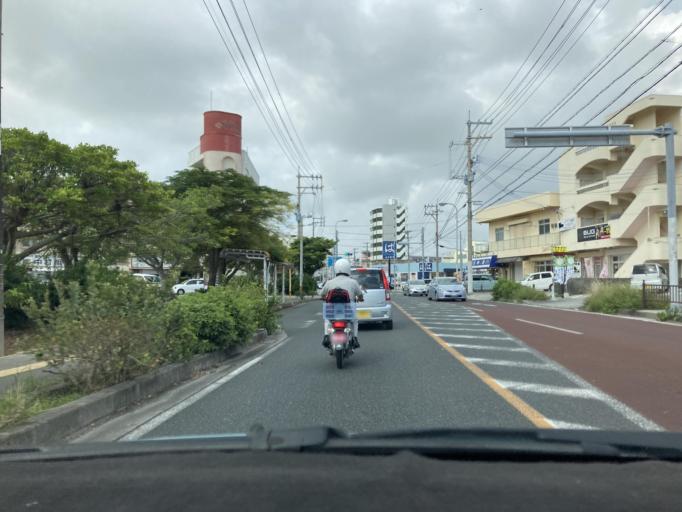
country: JP
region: Okinawa
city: Itoman
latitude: 26.1418
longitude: 127.6721
